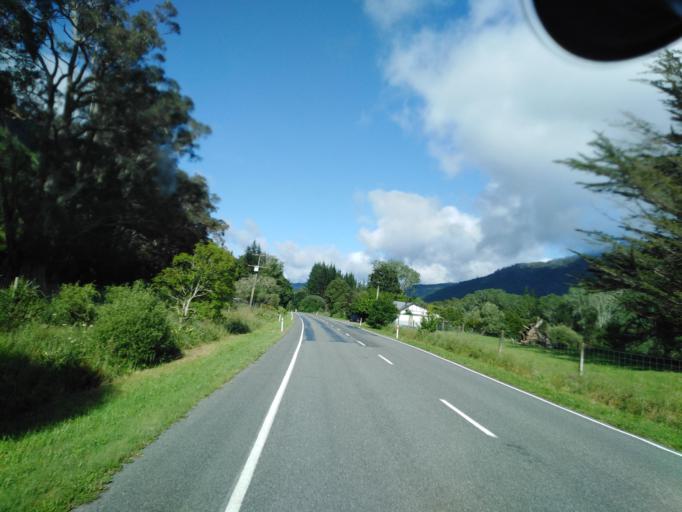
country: NZ
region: Nelson
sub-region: Nelson City
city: Nelson
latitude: -41.2996
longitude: 173.5863
